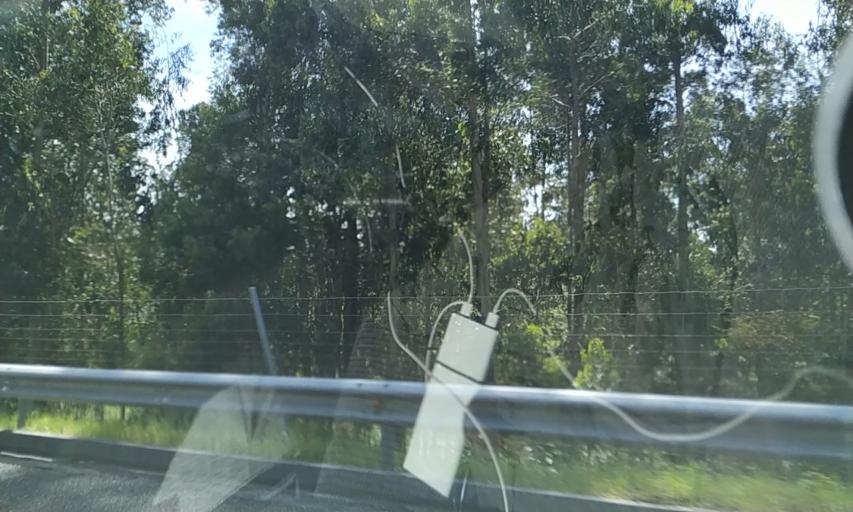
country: ES
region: Galicia
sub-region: Provincia de Pontevedra
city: Meano
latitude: 42.4593
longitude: -8.7779
